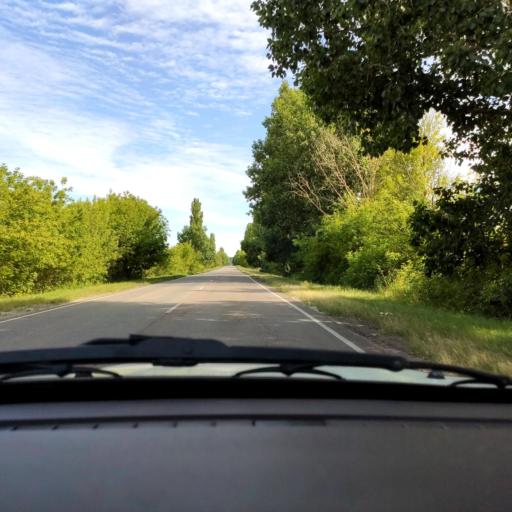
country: RU
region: Voronezj
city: Uglyanets
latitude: 51.8398
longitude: 39.6531
